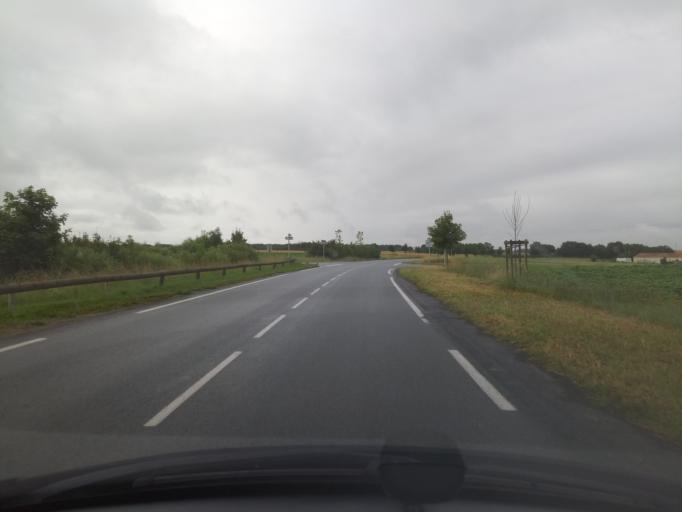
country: FR
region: Poitou-Charentes
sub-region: Departement de la Charente-Maritime
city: Courcon
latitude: 46.1881
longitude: -0.8550
